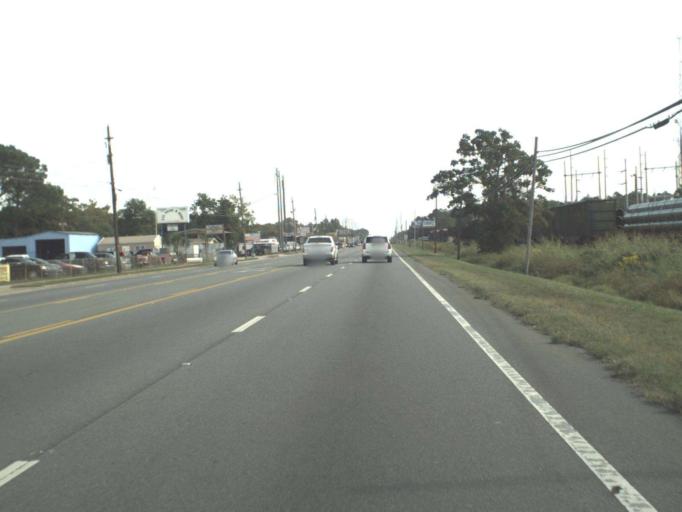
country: US
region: Florida
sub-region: Bay County
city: Hiland Park
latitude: 30.1931
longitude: -85.6356
